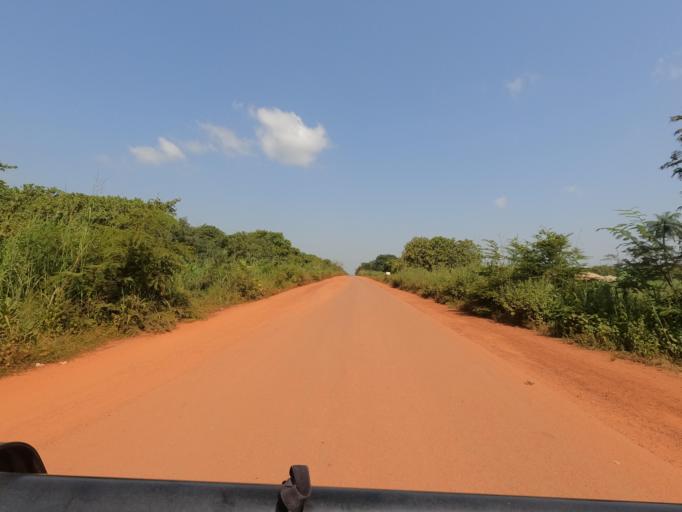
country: GW
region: Oio
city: Bissora
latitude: 12.3164
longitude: -15.7579
